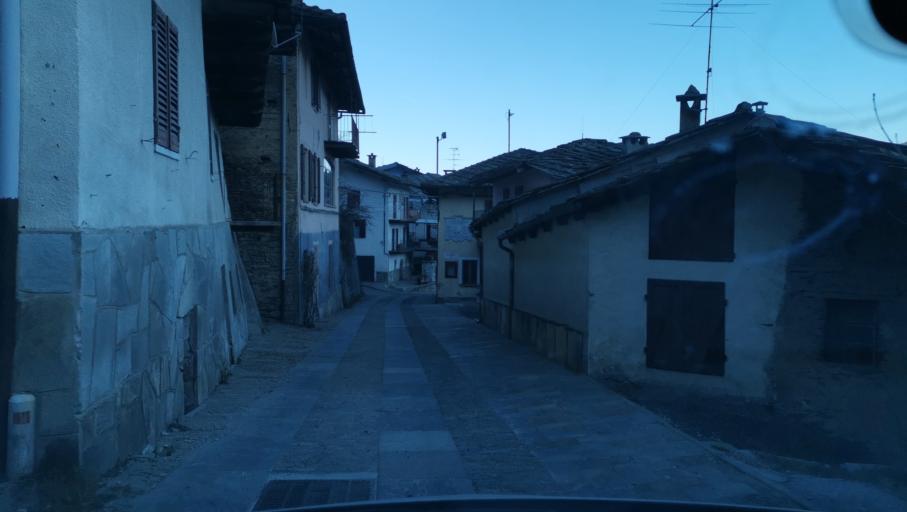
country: IT
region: Piedmont
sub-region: Provincia di Torino
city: Rora
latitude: 44.7925
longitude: 7.1980
